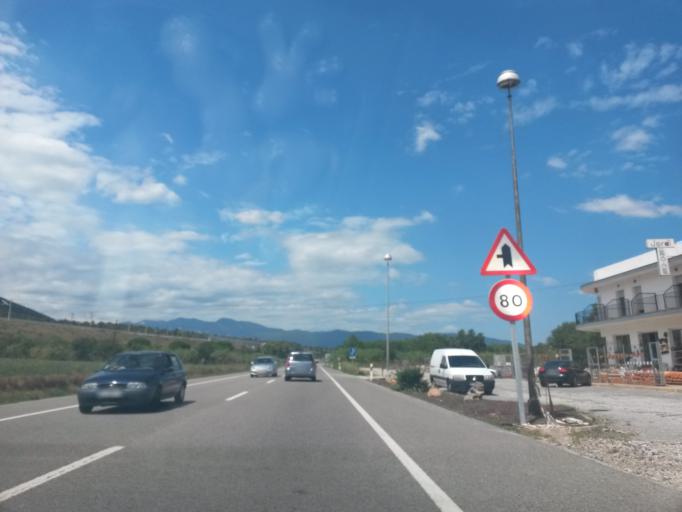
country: ES
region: Catalonia
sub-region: Provincia de Girona
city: Biure
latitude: 42.3487
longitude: 2.9098
